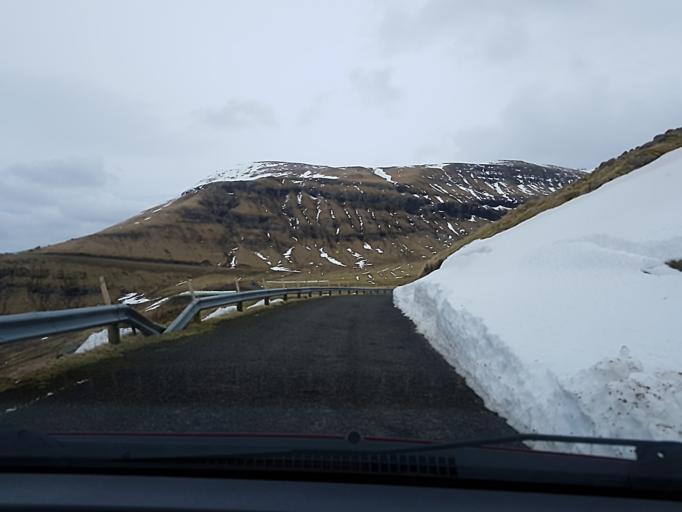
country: FO
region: Streymoy
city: Hoyvik
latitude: 61.9952
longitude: -6.8869
